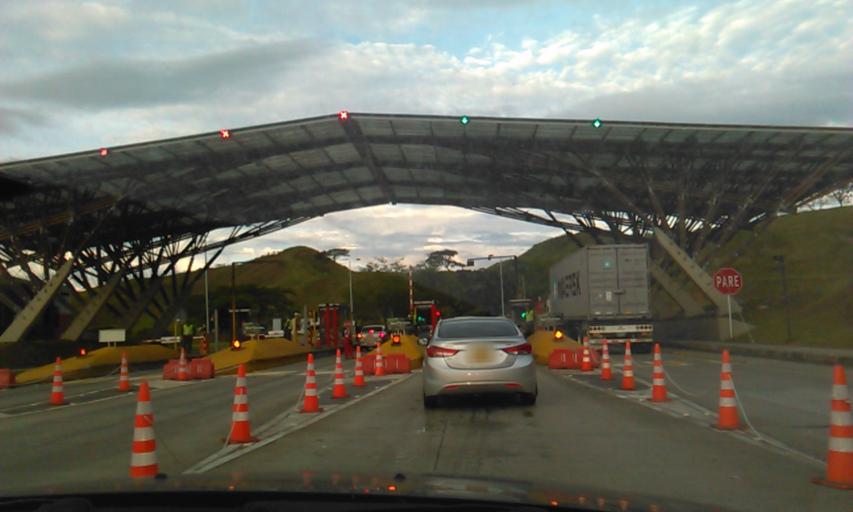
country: CO
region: Valle del Cauca
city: Caicedonia
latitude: 4.4082
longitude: -75.8997
